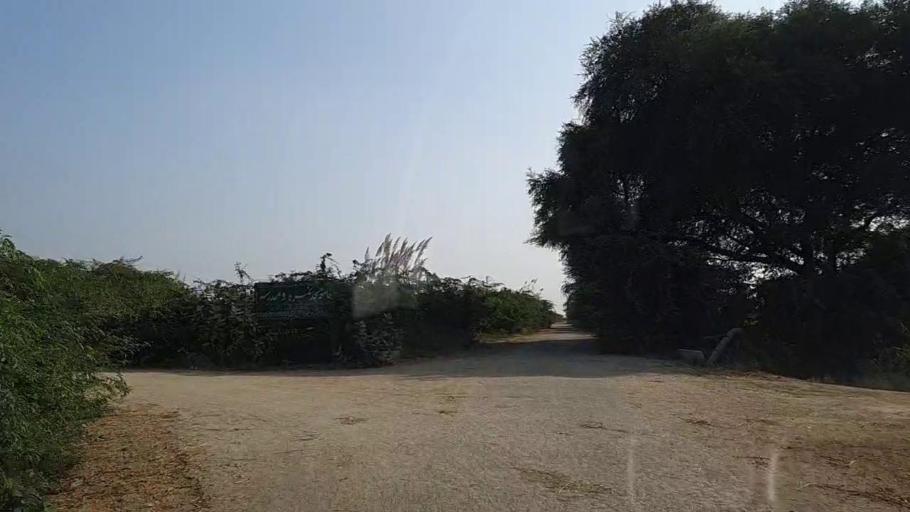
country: PK
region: Sindh
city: Mirpur Sakro
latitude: 24.6198
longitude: 67.6596
